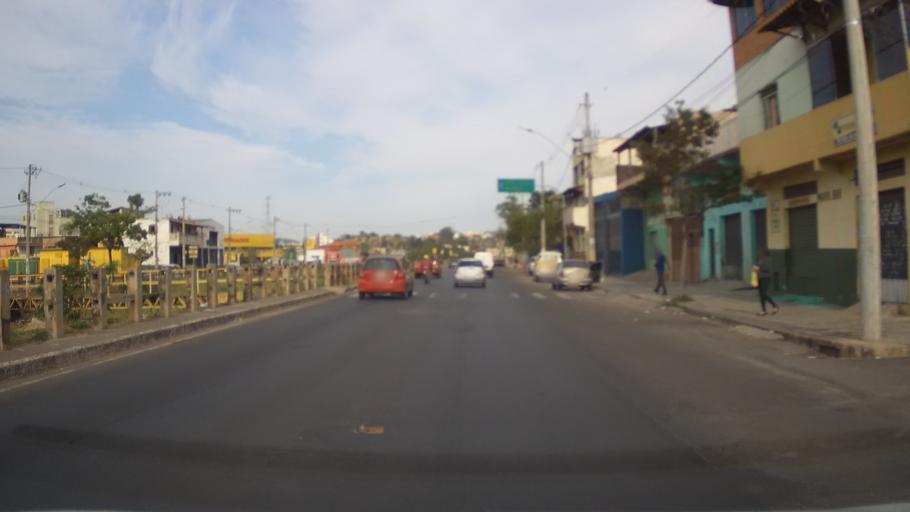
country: BR
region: Minas Gerais
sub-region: Contagem
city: Contagem
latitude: -19.8736
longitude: -44.0169
